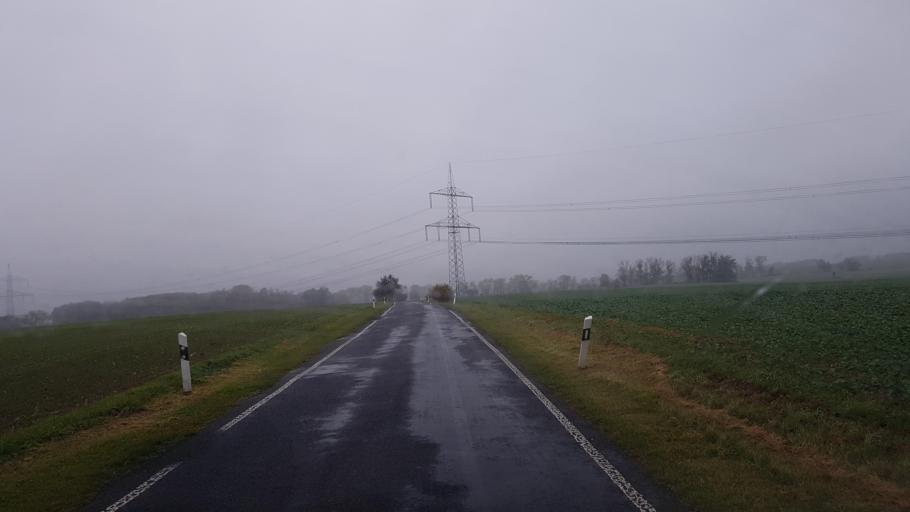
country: DE
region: Brandenburg
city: Furstenwalde
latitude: 52.4181
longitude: 14.0613
